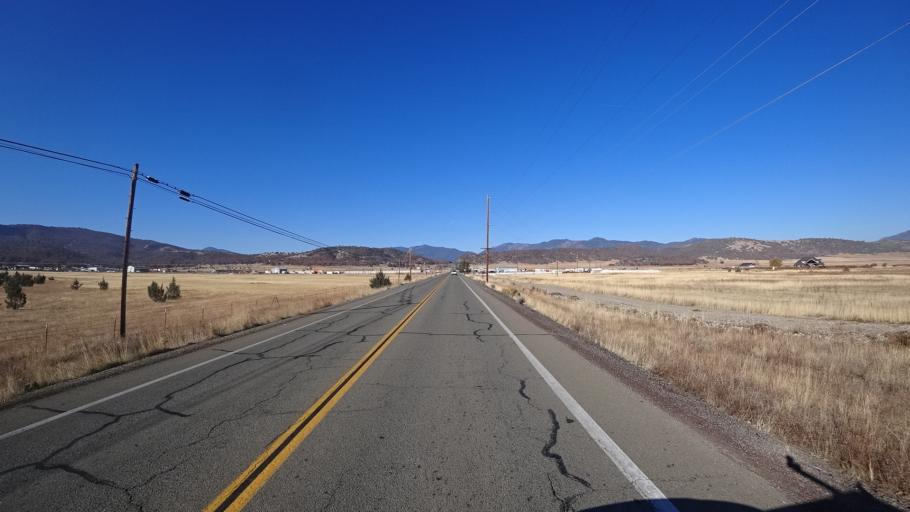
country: US
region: California
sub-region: Siskiyou County
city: Yreka
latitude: 41.7113
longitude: -122.5944
